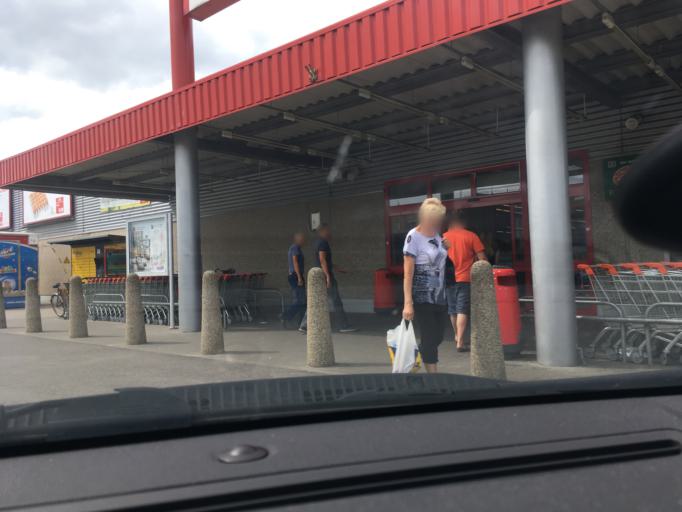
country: PL
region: Podlasie
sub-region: Powiat augustowski
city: Augustow
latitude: 53.8388
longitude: 22.9726
